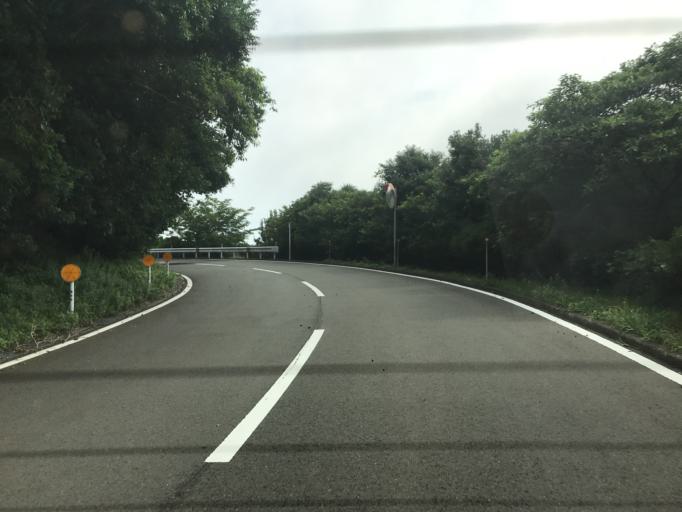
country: JP
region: Shizuoka
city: Ito
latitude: 34.7413
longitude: 139.4347
